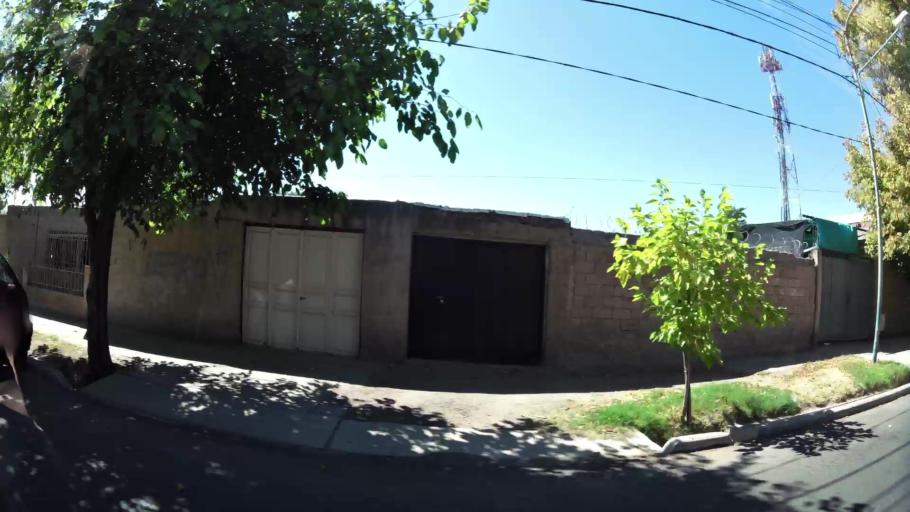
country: AR
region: Mendoza
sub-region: Departamento de Godoy Cruz
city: Godoy Cruz
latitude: -32.9120
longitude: -68.8641
